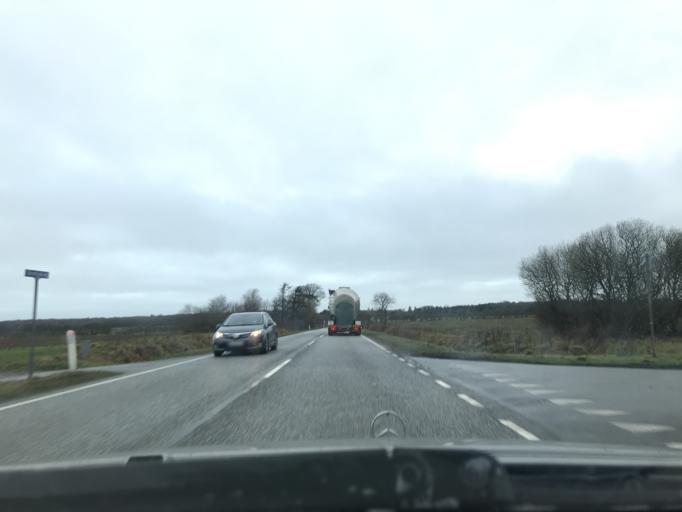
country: DK
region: South Denmark
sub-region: Haderslev Kommune
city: Gram
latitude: 55.2318
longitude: 8.9495
